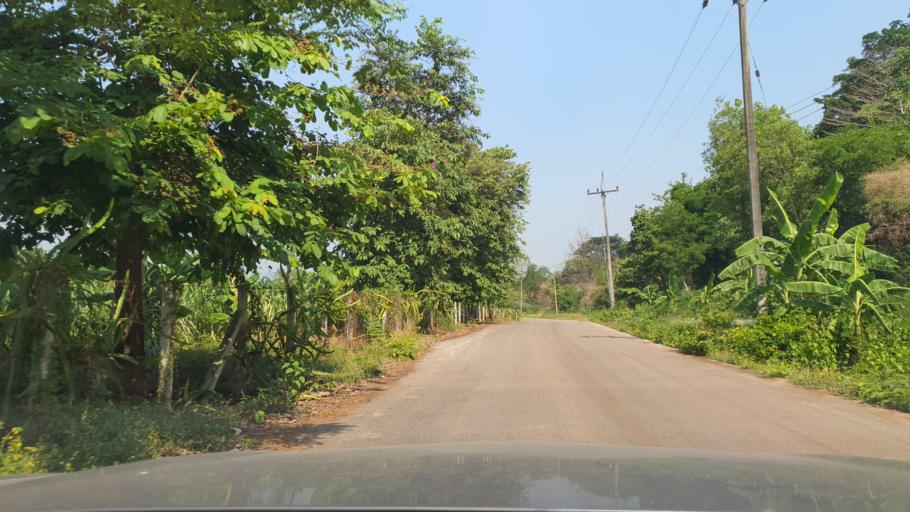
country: TH
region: Kanchanaburi
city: Sai Yok
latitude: 14.0977
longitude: 99.1730
